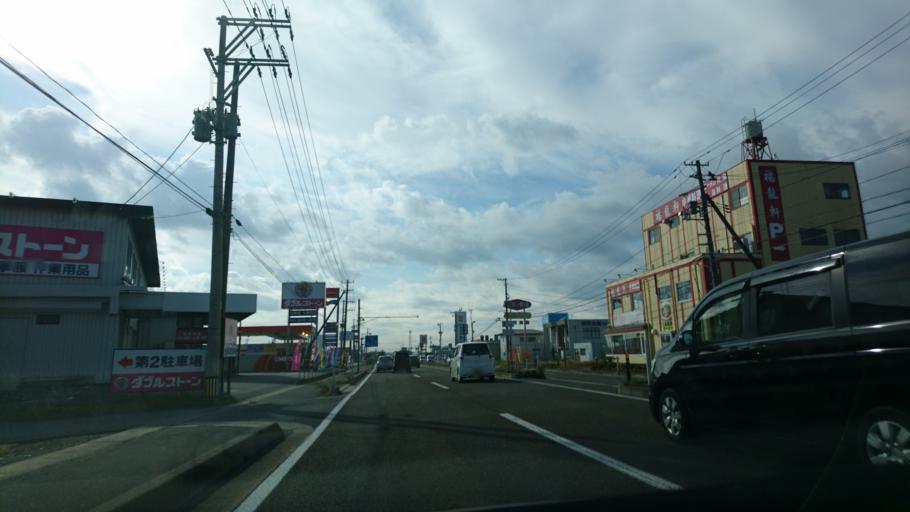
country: JP
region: Miyagi
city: Furukawa
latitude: 38.5769
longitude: 140.9460
